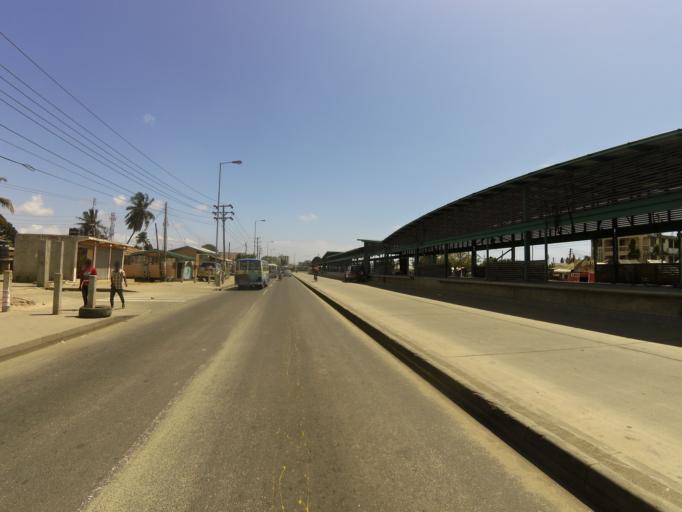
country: TZ
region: Dar es Salaam
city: Magomeni
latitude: -6.7959
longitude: 39.2640
